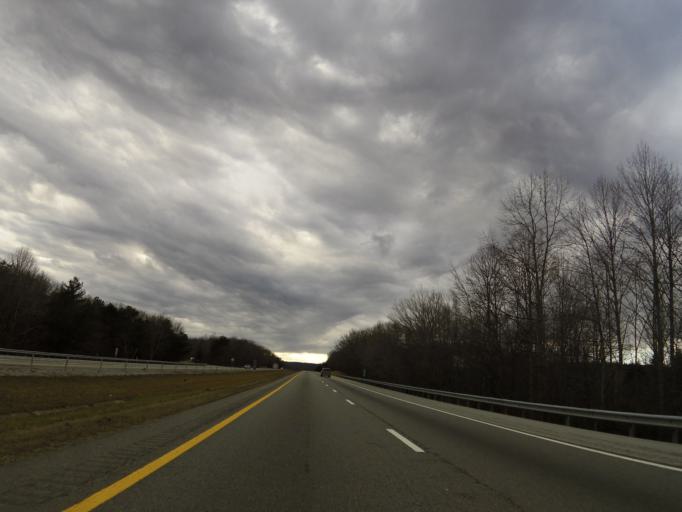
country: US
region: Tennessee
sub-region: Roane County
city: Rockwood
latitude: 35.9015
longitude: -84.7753
